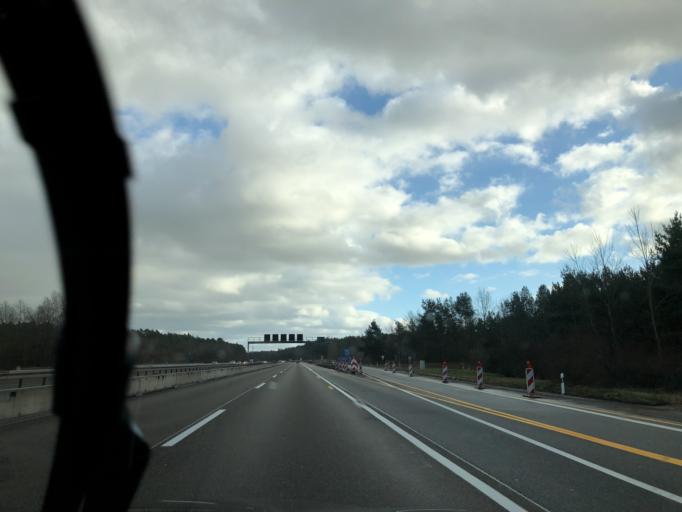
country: DE
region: Bavaria
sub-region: Regierungsbezirk Unterfranken
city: Kleinostheim
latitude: 49.9941
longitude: 9.0123
